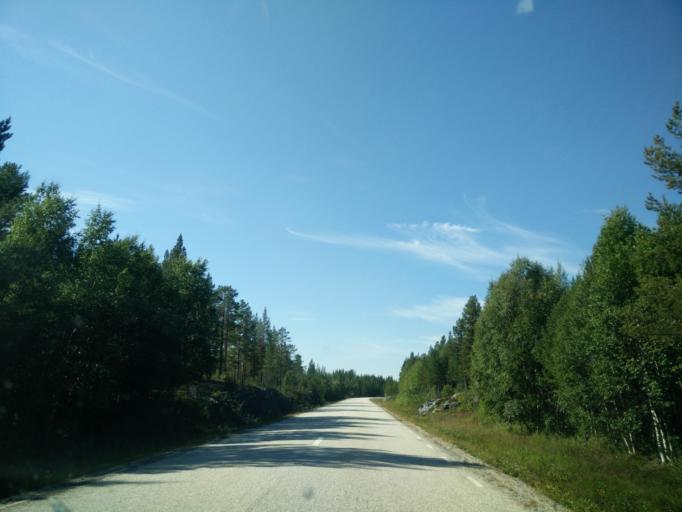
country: SE
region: Jaemtland
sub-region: Are Kommun
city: Jarpen
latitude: 62.8262
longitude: 13.4729
